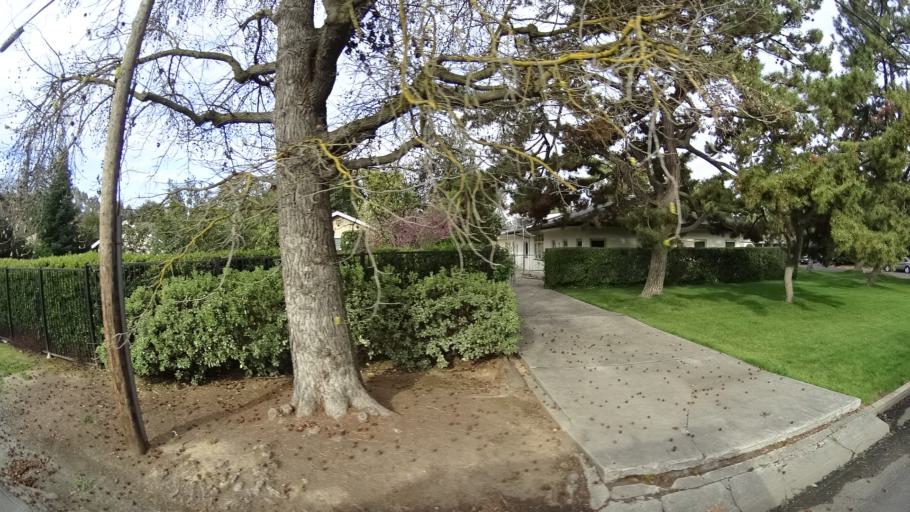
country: US
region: California
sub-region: Fresno County
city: Fresno
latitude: 36.8046
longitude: -119.7995
